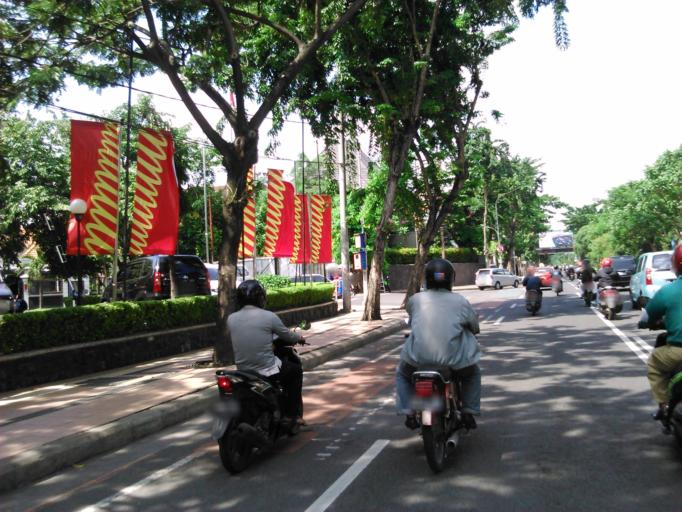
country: ID
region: East Java
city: Gubengairlangga
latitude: -7.2822
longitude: 112.7405
